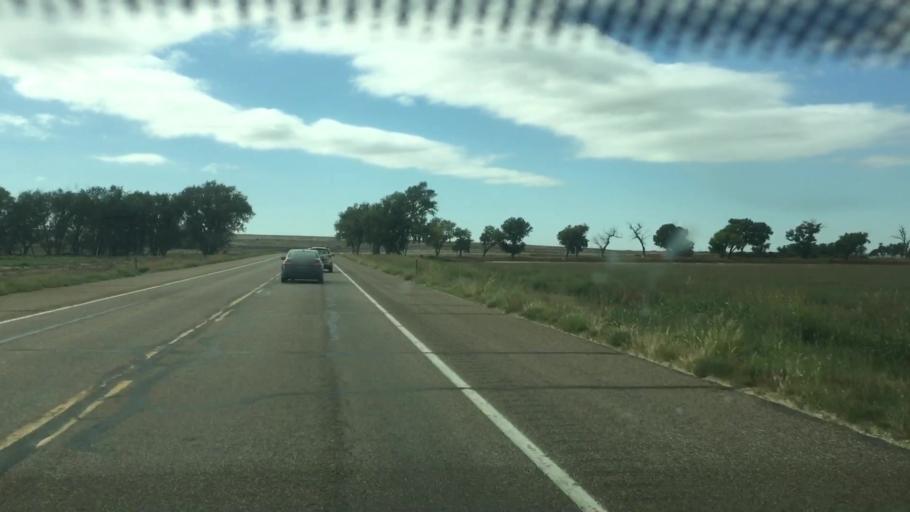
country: US
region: Colorado
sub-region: Prowers County
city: Lamar
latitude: 38.0637
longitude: -102.3532
